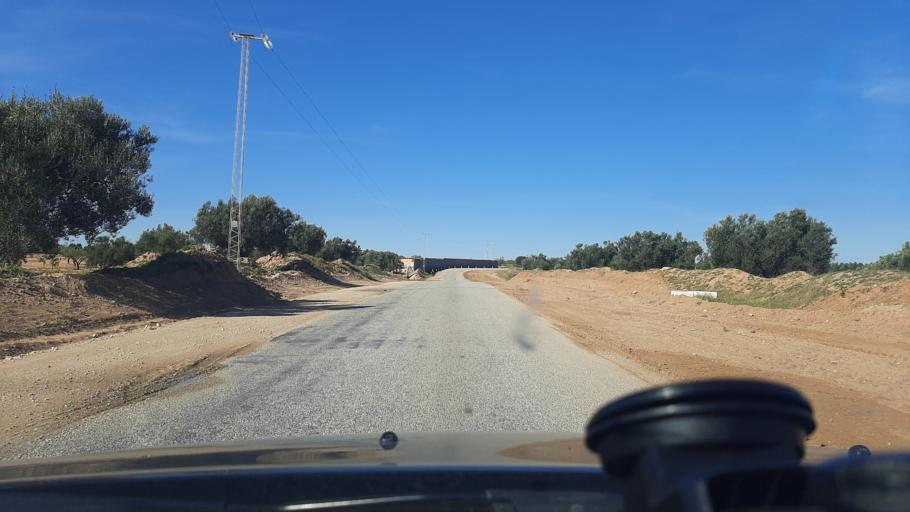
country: TN
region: Safaqis
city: Sfax
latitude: 34.9099
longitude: 10.5910
